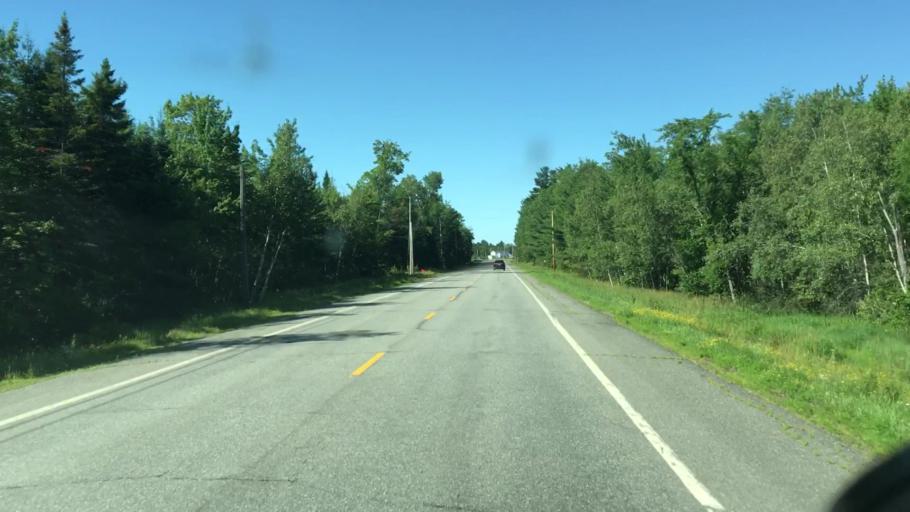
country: US
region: Maine
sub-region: Penobscot County
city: Enfield
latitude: 45.3032
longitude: -68.6147
